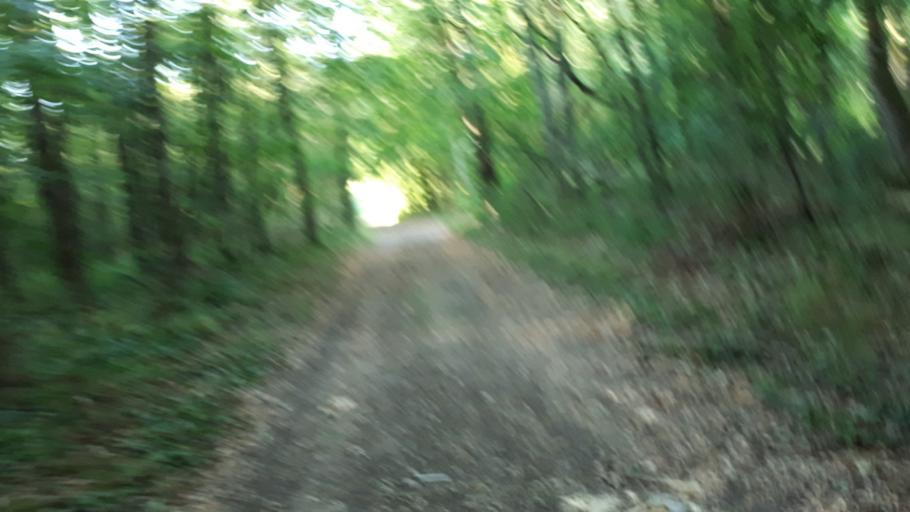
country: FR
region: Centre
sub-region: Departement du Loir-et-Cher
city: Villiers-sur-Loir
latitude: 47.7924
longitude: 0.9799
